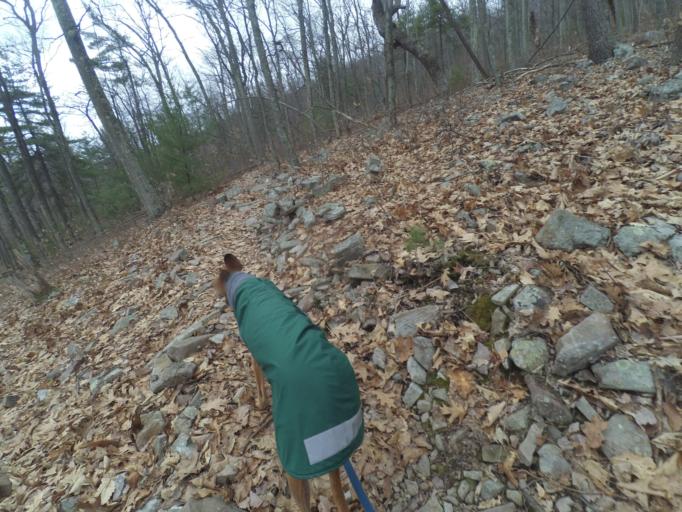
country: US
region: Pennsylvania
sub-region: Centre County
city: Boalsburg
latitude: 40.7627
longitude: -77.7112
